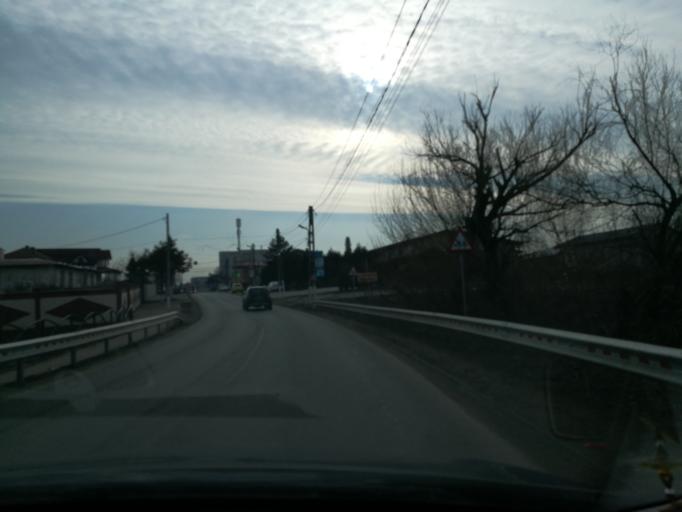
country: RO
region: Ilfov
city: Stefanestii de Jos
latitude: 44.5368
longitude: 26.2004
